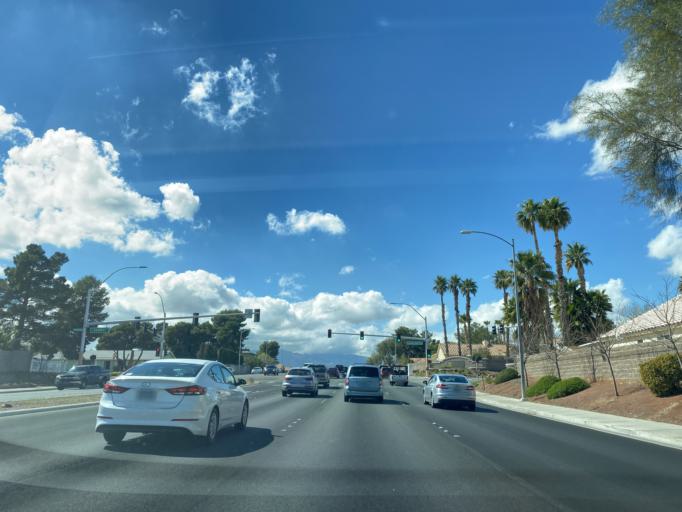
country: US
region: Nevada
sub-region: Clark County
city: Las Vegas
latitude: 36.2390
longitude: -115.2188
